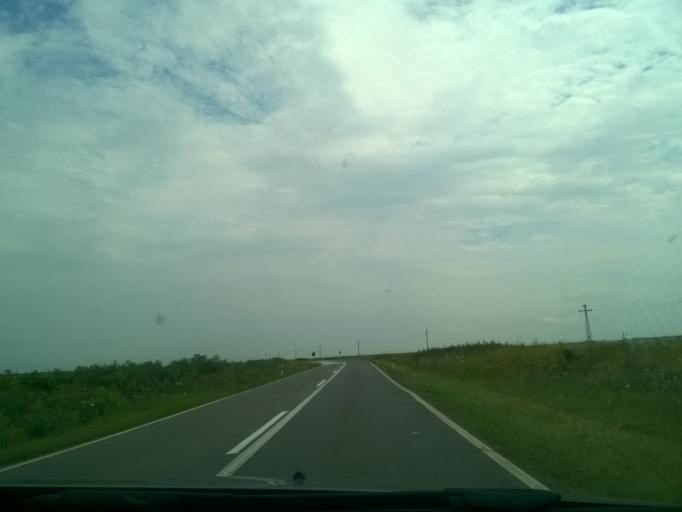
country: RS
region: Autonomna Pokrajina Vojvodina
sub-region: Srednjebanatski Okrug
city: Secanj
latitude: 45.3495
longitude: 20.7802
